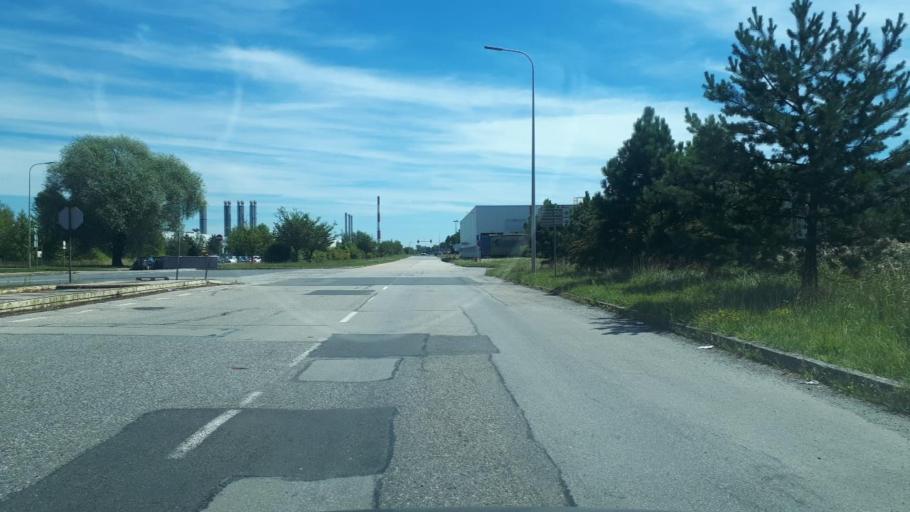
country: PL
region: Silesian Voivodeship
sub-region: Powiat bierunsko-ledzinski
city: Bierun
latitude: 50.1055
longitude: 19.0625
